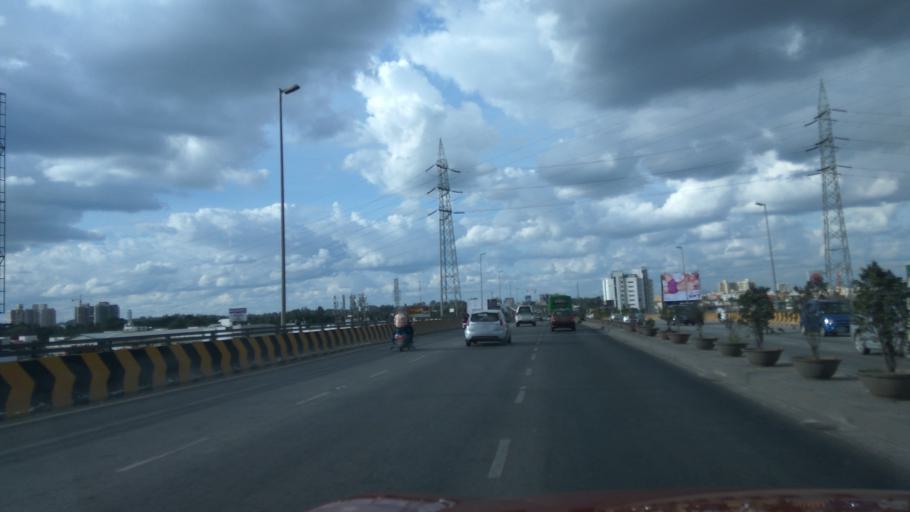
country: IN
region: Karnataka
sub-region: Bangalore Urban
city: Yelahanka
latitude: 13.0570
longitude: 77.5934
